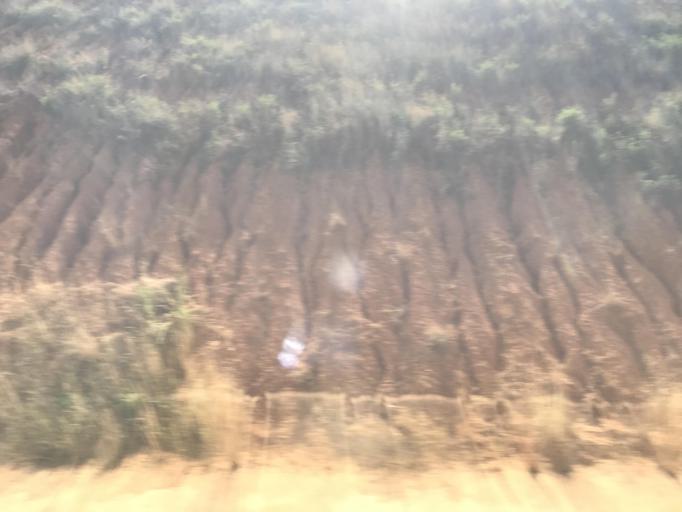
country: ES
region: Aragon
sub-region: Provincia de Zaragoza
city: Cabolafuente
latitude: 41.2374
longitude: -2.0100
